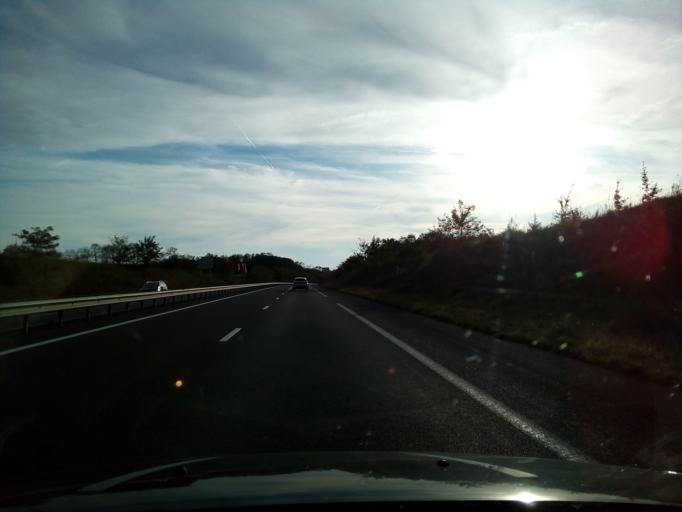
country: FR
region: Poitou-Charentes
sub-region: Departement de la Charente
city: La Rochefoucauld
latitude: 45.7601
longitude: 0.3932
